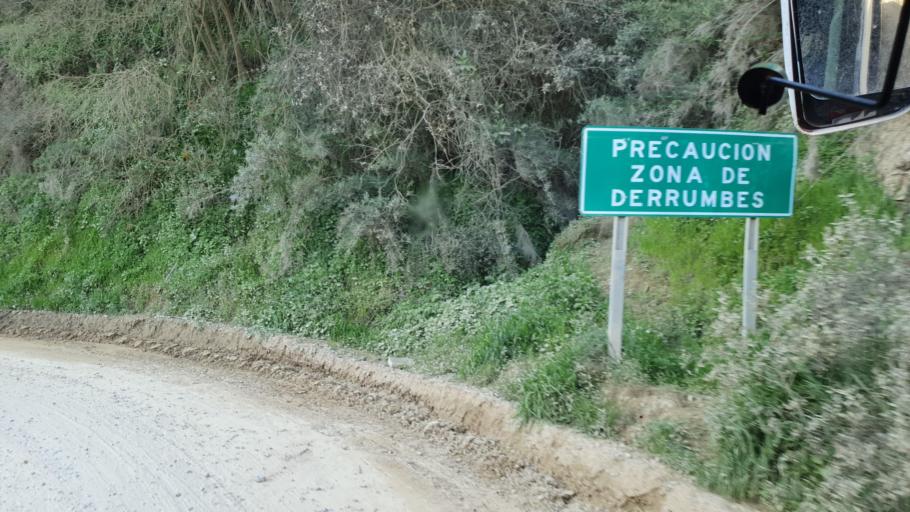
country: CL
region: Valparaiso
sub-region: Provincia de Marga Marga
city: Limache
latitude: -33.1981
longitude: -71.2625
